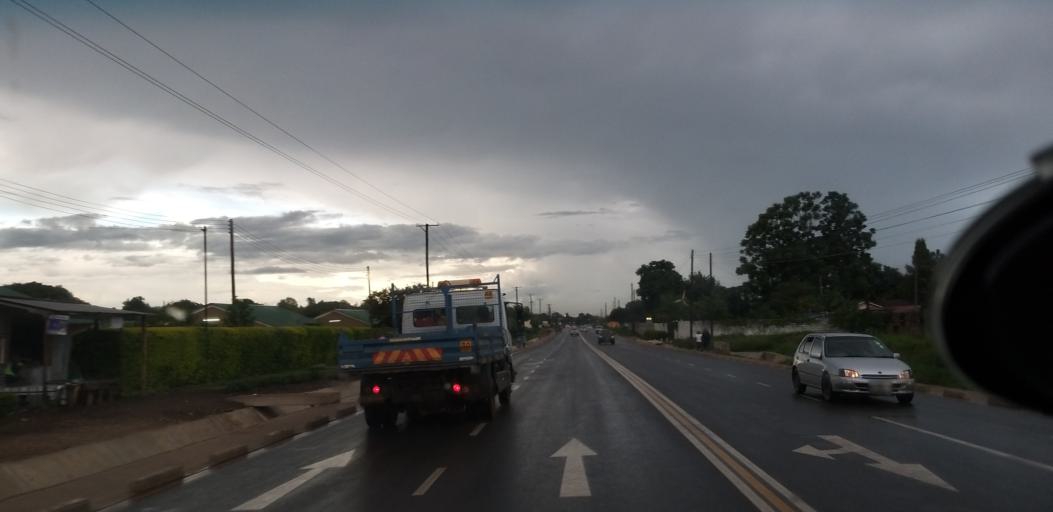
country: ZM
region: Lusaka
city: Lusaka
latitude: -15.4274
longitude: 28.3561
